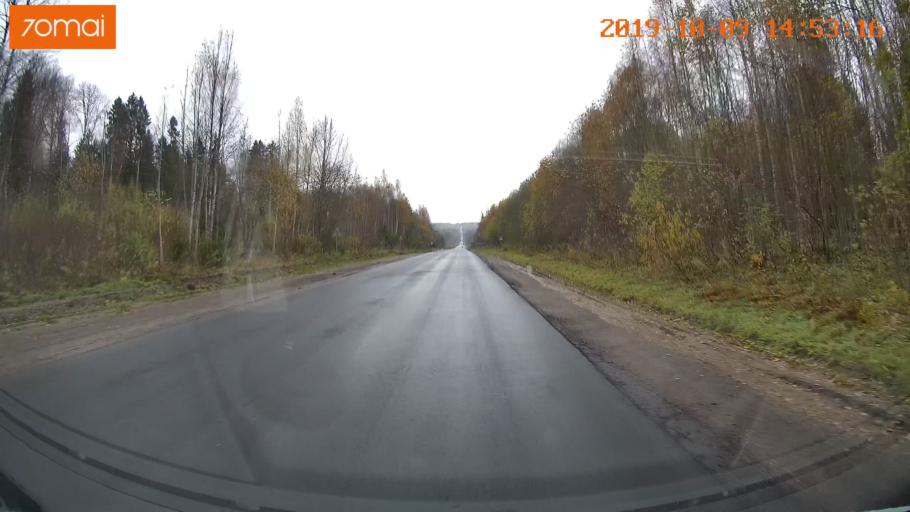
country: RU
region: Kostroma
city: Chistyye Bory
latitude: 58.3698
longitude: 41.6374
